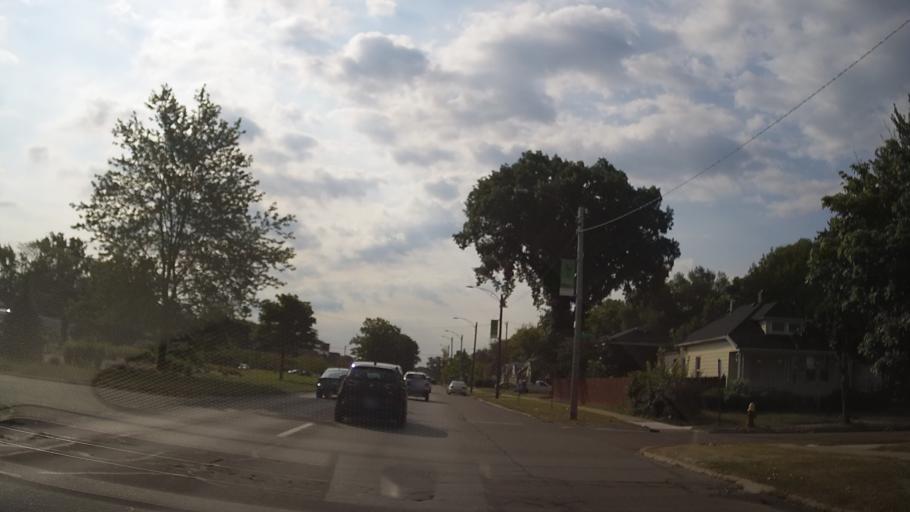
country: US
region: Michigan
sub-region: Wayne County
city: Harper Woods
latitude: 42.4216
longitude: -82.9224
